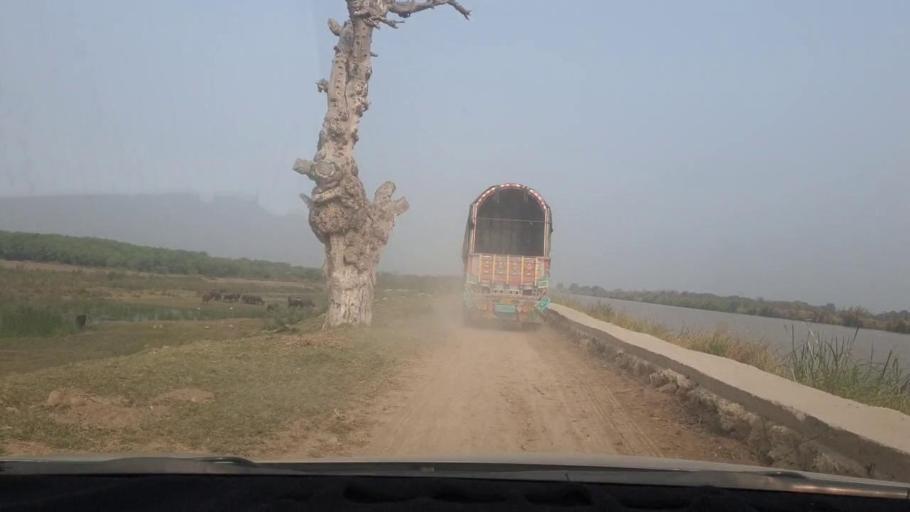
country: PK
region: Sindh
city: Matiari
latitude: 25.6558
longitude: 68.5610
